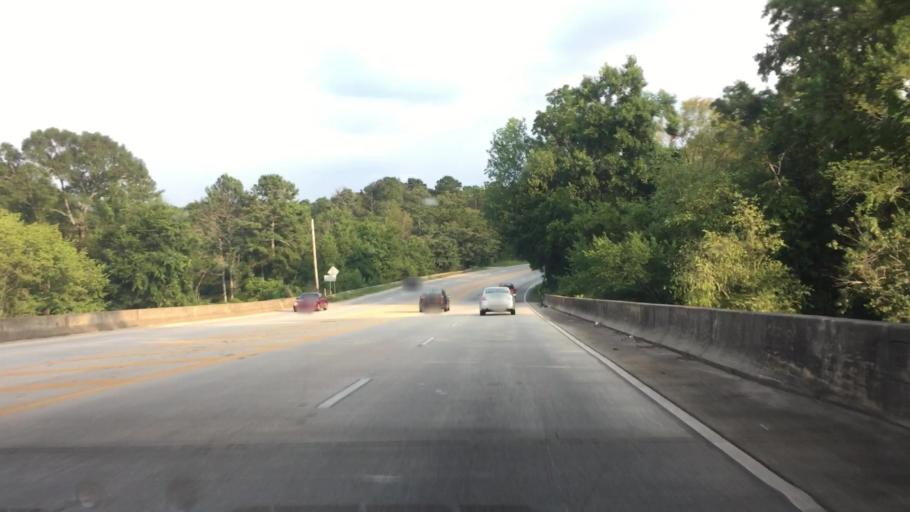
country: US
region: Georgia
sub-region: DeKalb County
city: Pine Mountain
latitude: 33.6535
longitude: -84.1879
